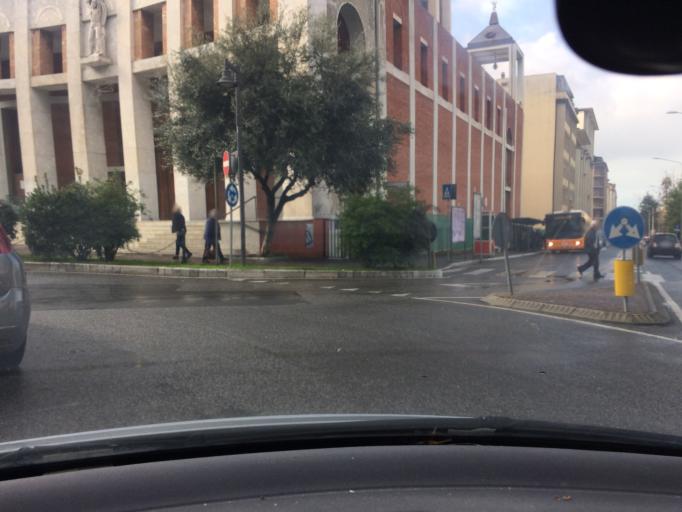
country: IT
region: Tuscany
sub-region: Provincia di Massa-Carrara
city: Massa
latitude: 44.0375
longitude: 10.1394
